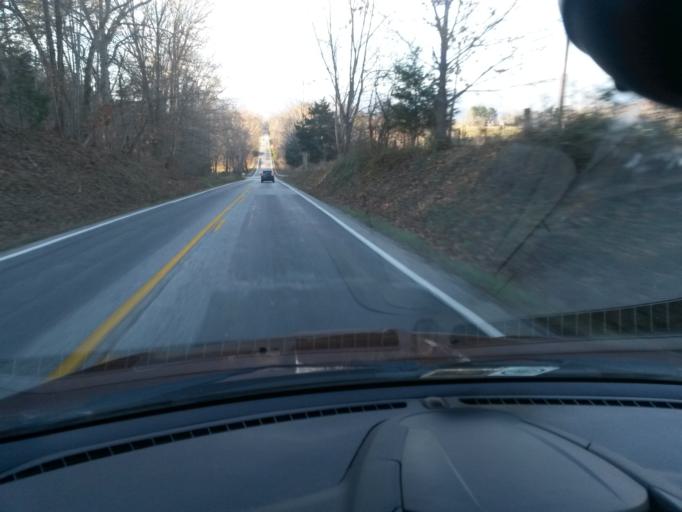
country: US
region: Virginia
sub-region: Amherst County
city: Amherst
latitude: 37.6447
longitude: -79.1251
